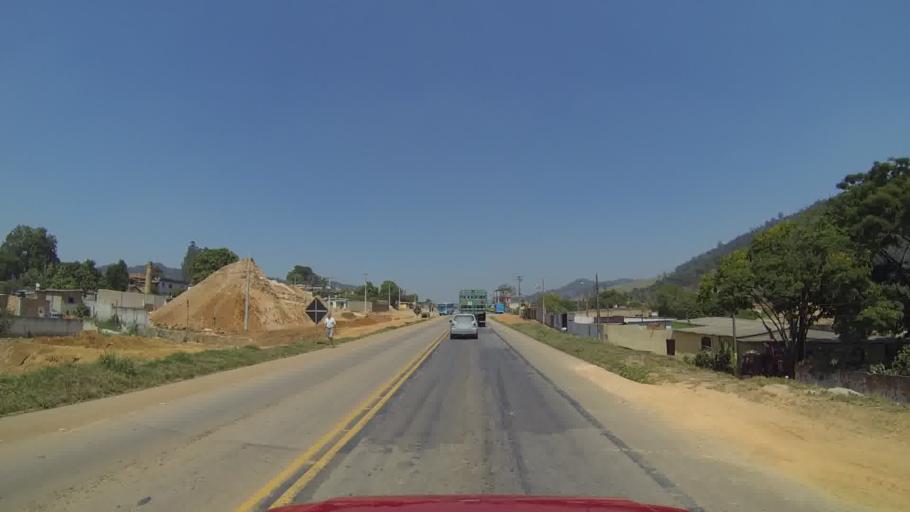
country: BR
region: Minas Gerais
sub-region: Mateus Leme
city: Mateus Leme
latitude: -20.0118
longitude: -44.4762
